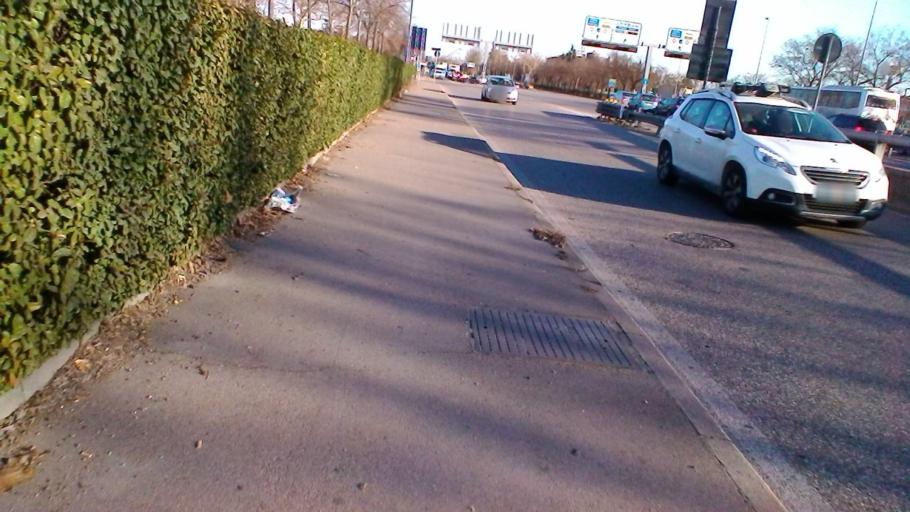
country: IT
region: Veneto
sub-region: Provincia di Verona
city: Verona
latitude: 45.4319
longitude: 10.9820
